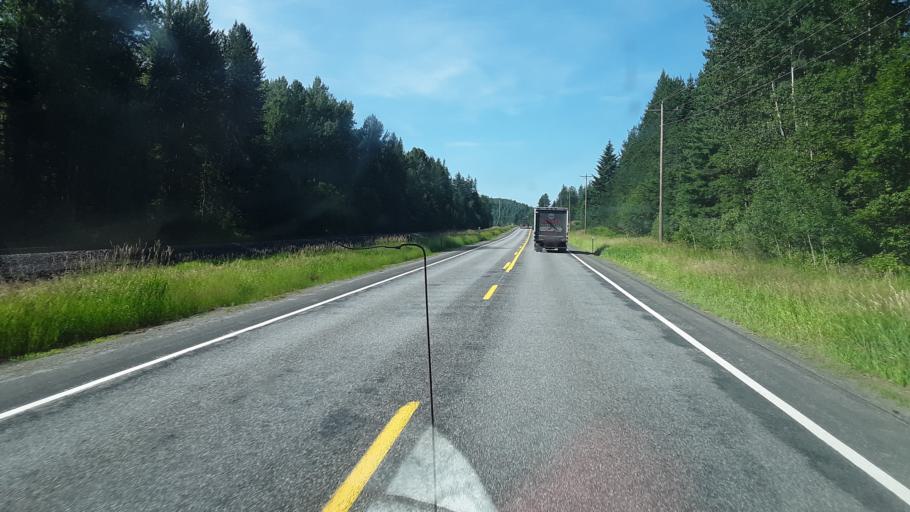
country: US
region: Idaho
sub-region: Bonner County
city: Ponderay
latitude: 48.4389
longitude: -116.4876
